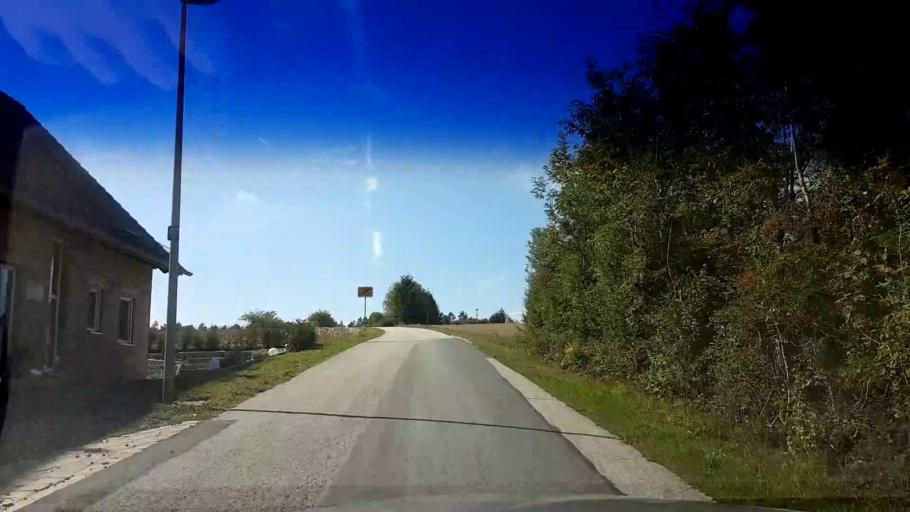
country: DE
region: Bavaria
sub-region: Upper Franconia
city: Poxdorf
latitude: 49.8744
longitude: 11.0901
